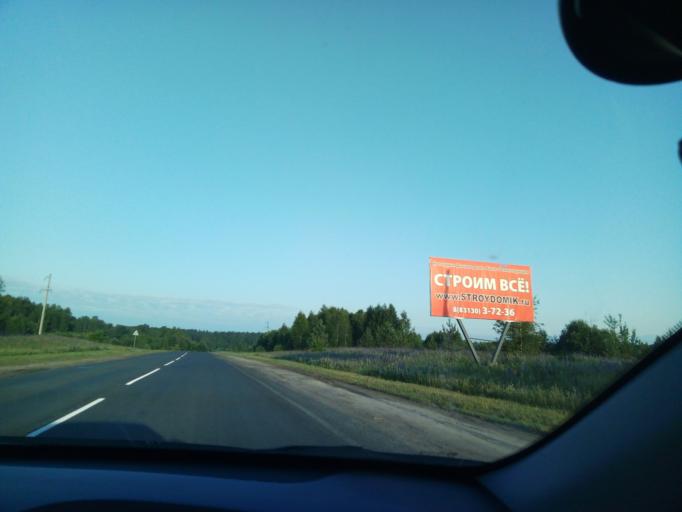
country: RU
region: Nizjnij Novgorod
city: Satis
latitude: 54.9361
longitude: 43.2350
